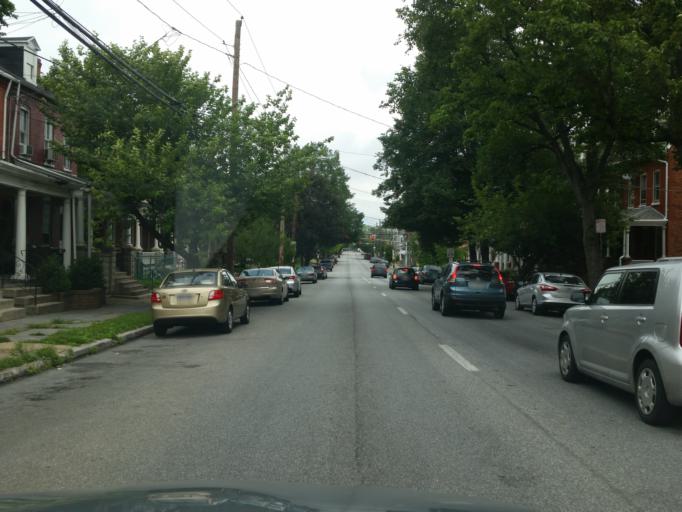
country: US
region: Pennsylvania
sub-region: Lancaster County
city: Lancaster
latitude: 40.0494
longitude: -76.3035
